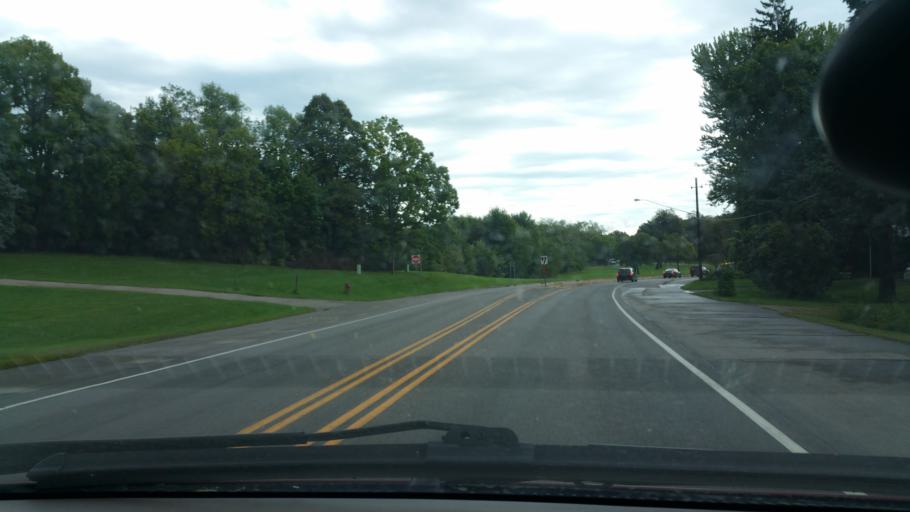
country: US
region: Minnesota
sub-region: Rice County
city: Northfield
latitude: 44.4568
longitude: -93.1822
